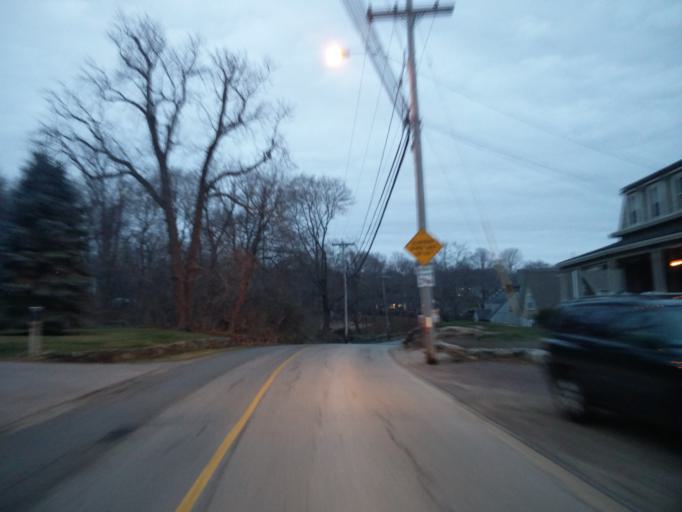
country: US
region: Massachusetts
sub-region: Norfolk County
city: Cohasset
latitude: 42.2634
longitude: -70.8303
